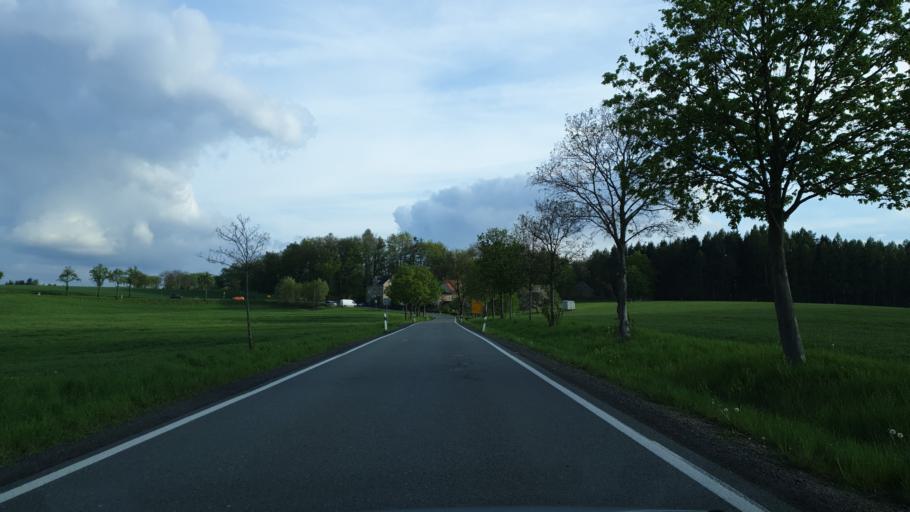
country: DE
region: Saxony
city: Lichtenstein
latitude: 50.7381
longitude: 12.6343
